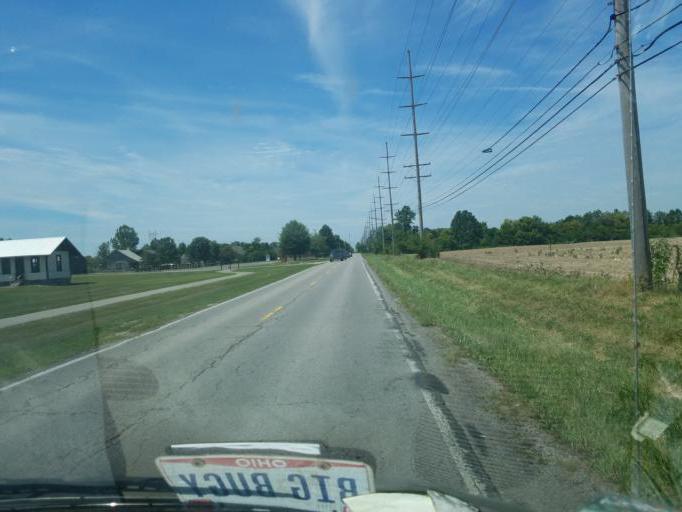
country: US
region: Ohio
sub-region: Franklin County
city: Grove City
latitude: 39.8603
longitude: -83.1014
